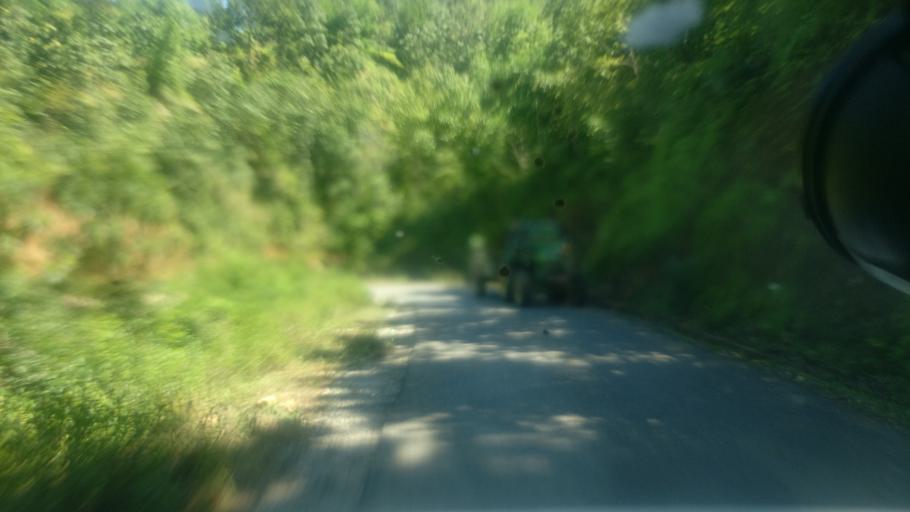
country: NP
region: Western Region
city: Baglung
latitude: 28.1754
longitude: 83.6608
